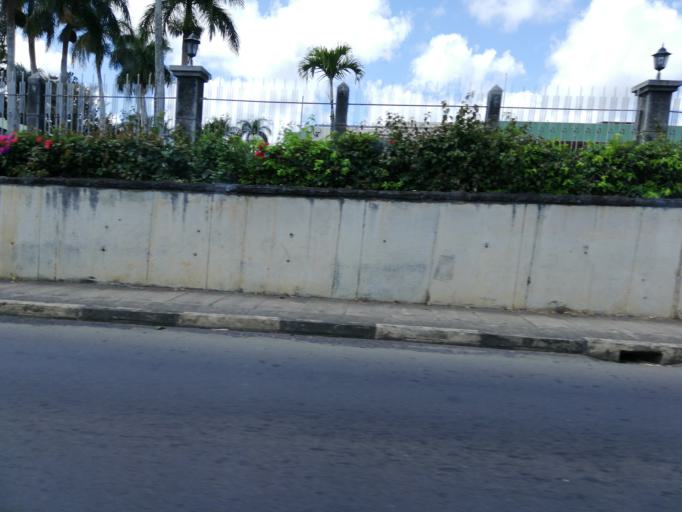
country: MU
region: Plaines Wilhems
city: Ebene
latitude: -20.2515
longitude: 57.4922
